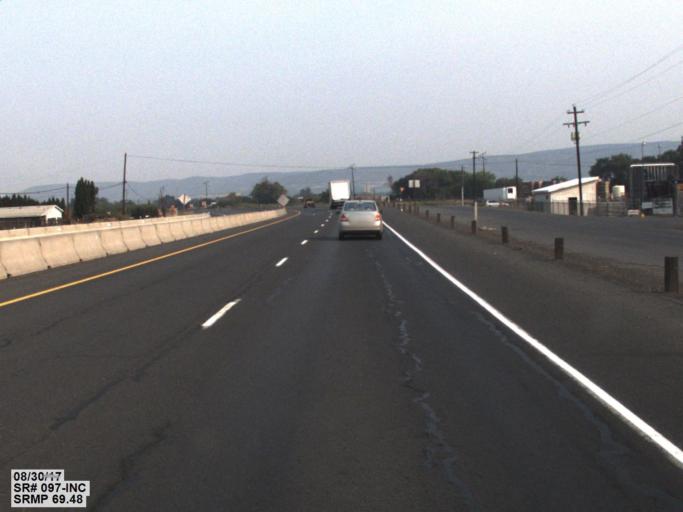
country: US
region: Washington
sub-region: Yakima County
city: Wapato
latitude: 46.4533
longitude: -120.4301
